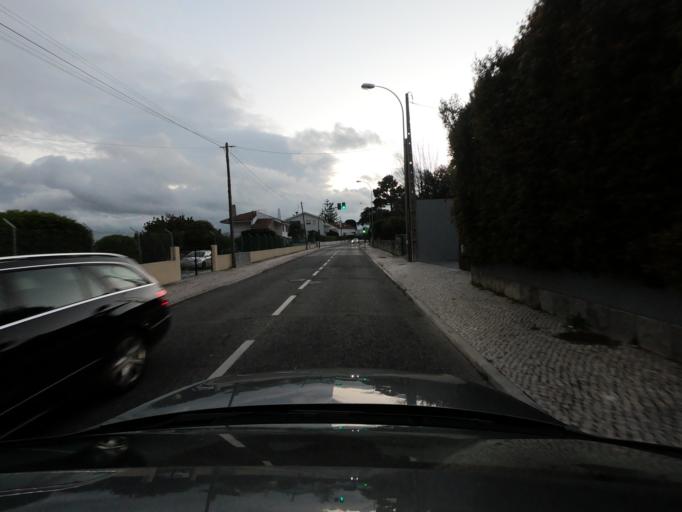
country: PT
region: Lisbon
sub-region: Oeiras
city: Paco de Arcos
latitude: 38.6976
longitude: -9.2870
